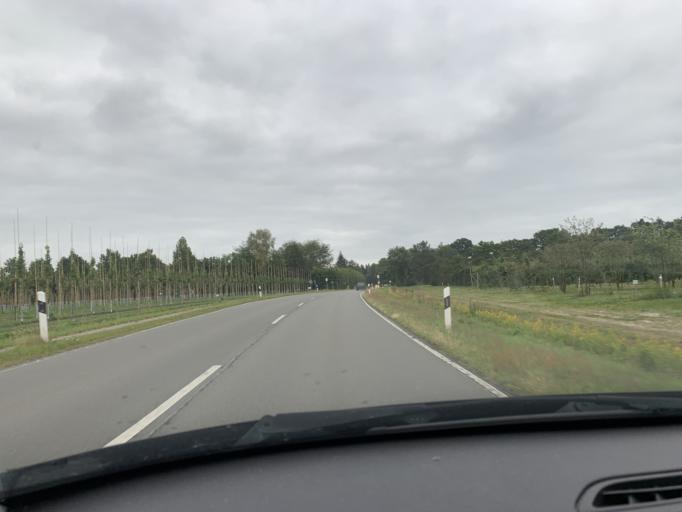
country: DE
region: Lower Saxony
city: Bad Zwischenahn
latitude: 53.2393
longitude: 7.9867
